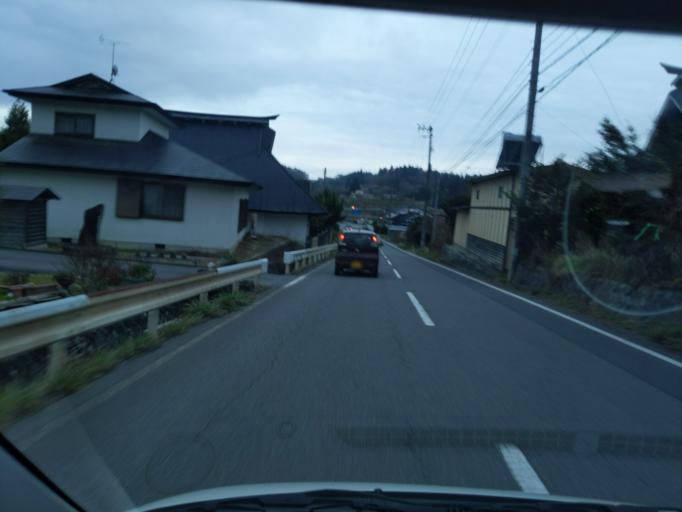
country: JP
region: Iwate
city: Ichinoseki
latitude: 39.0227
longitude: 141.3310
